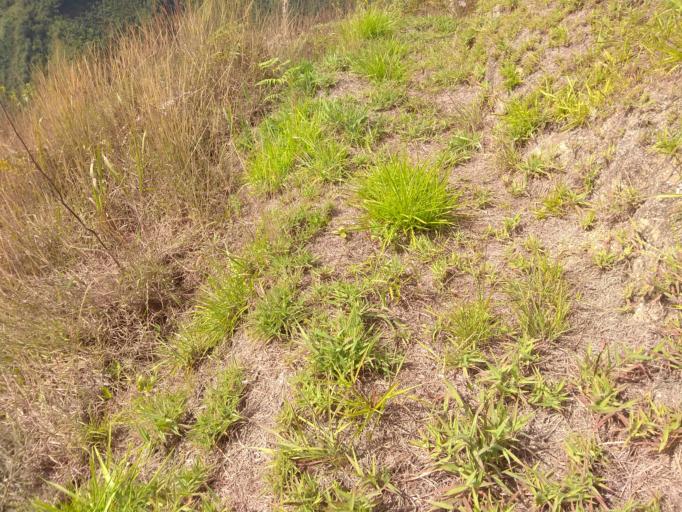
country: PE
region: Junin
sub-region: Chanchamayo
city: San Ramon
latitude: -11.3119
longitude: -75.3096
